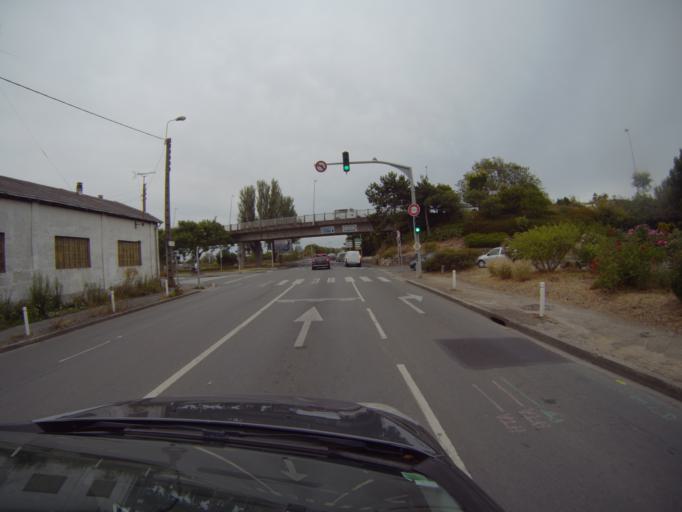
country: FR
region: Poitou-Charentes
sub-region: Departement de la Charente-Maritime
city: La Rochelle
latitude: 46.1573
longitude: -1.1425
